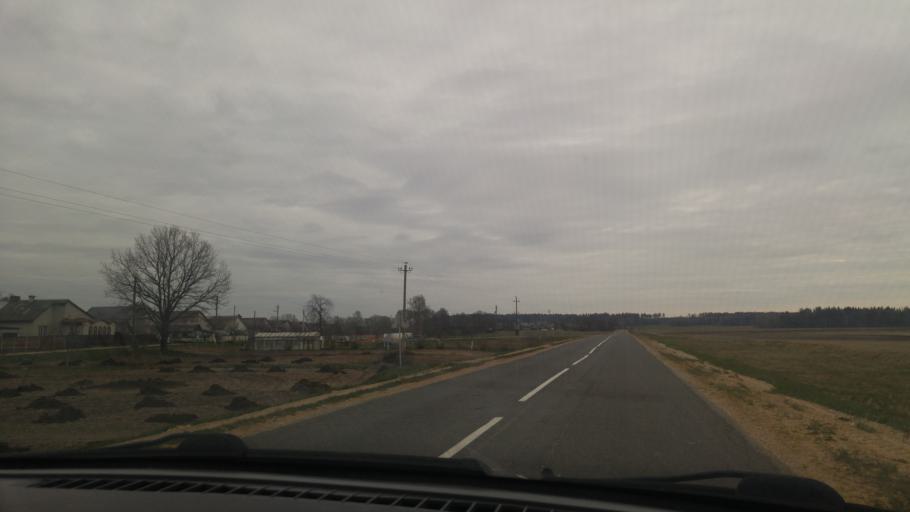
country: BY
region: Minsk
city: Chervyen'
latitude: 53.7260
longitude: 28.2688
